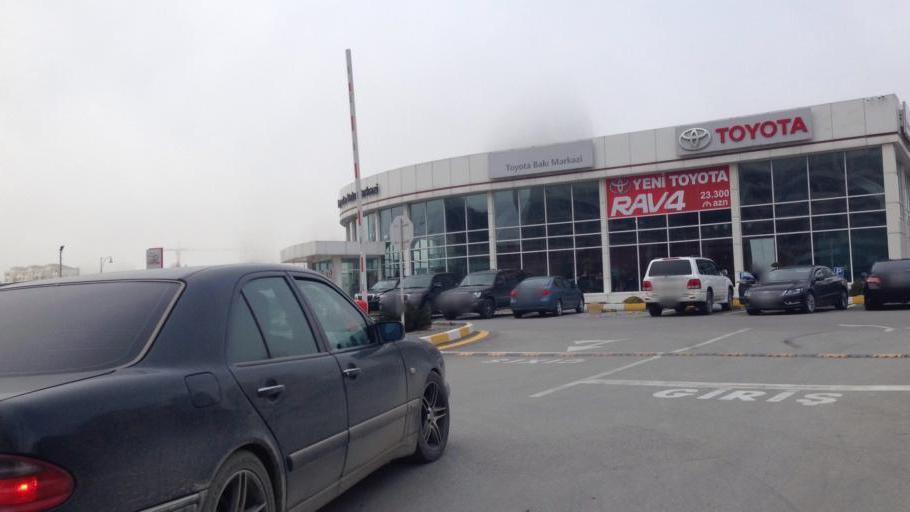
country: AZ
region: Baki
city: Baku
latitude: 40.3856
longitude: 49.8681
